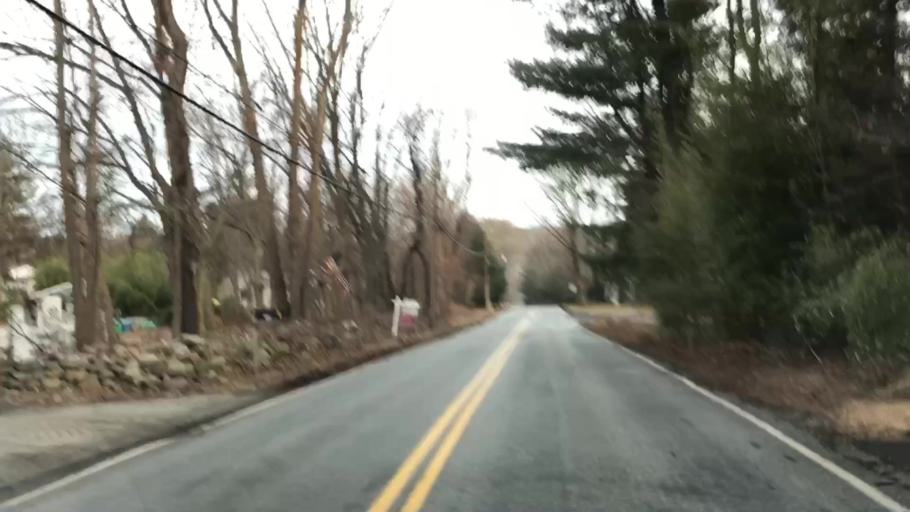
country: US
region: New York
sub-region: Rockland County
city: Viola
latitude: 41.1436
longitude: -74.0981
